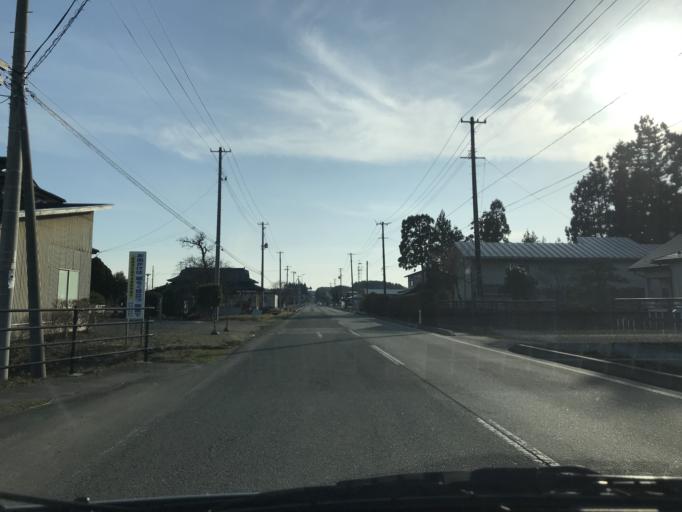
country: JP
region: Iwate
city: Kitakami
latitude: 39.2482
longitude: 141.1047
